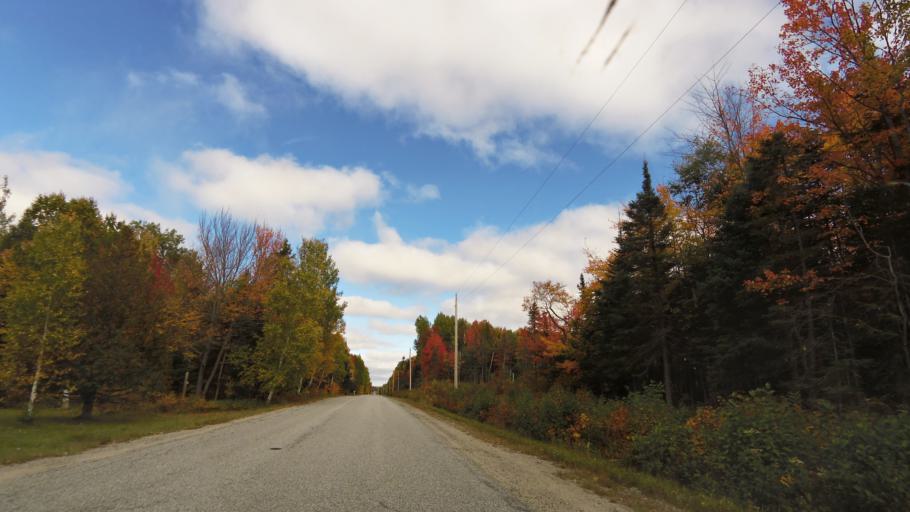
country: CA
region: Ontario
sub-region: Nipissing District
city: North Bay
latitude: 46.3546
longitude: -79.4871
